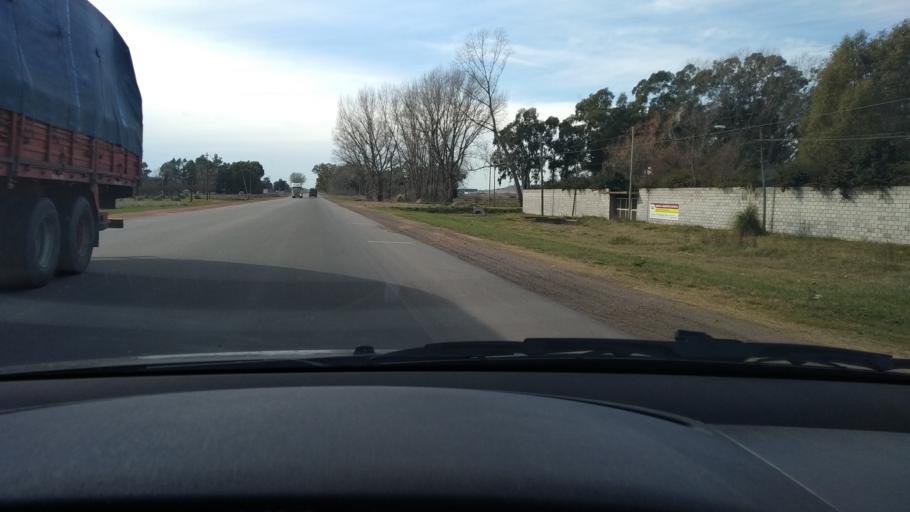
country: AR
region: Buenos Aires
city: Olavarria
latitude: -36.9515
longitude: -60.2486
